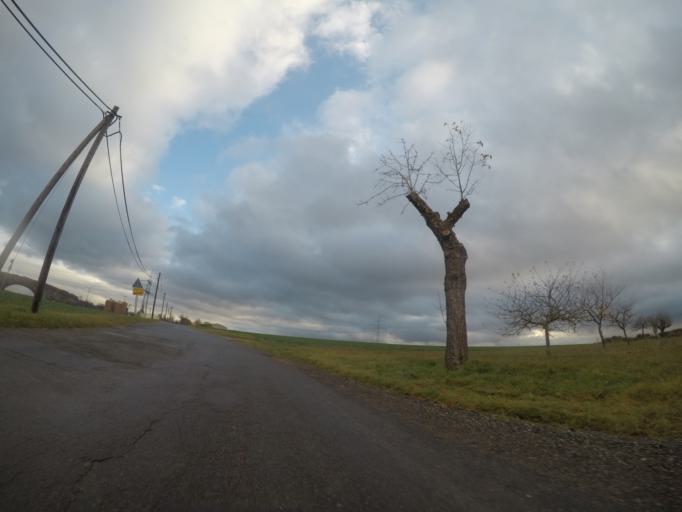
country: DE
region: Thuringia
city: Vollmershain
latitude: 50.8486
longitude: 12.3088
